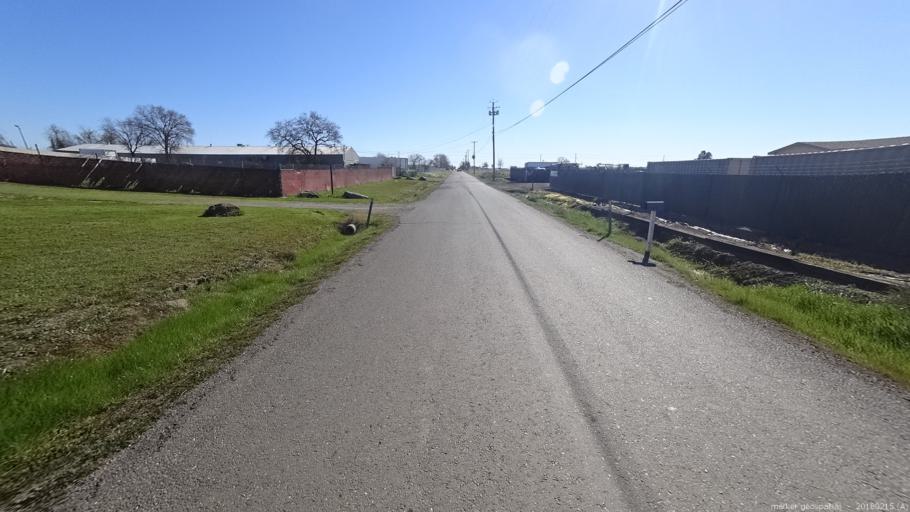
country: US
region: California
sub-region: Sacramento County
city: North Highlands
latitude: 38.7001
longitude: -121.3968
